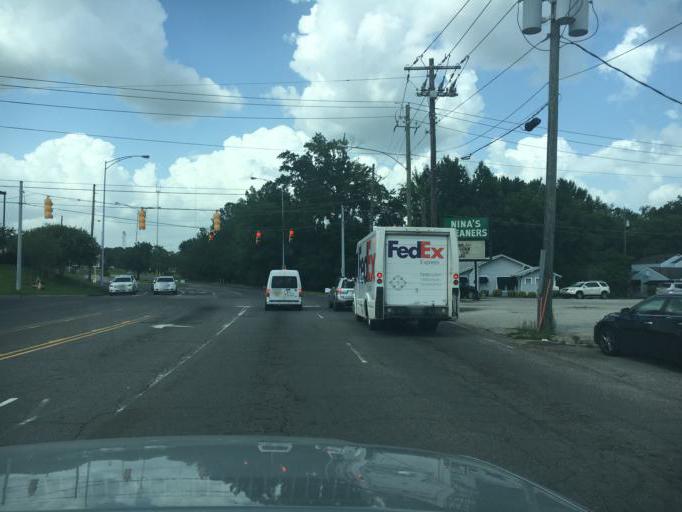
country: US
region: Alabama
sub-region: Jefferson County
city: Homewood
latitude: 33.4662
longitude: -86.8209
